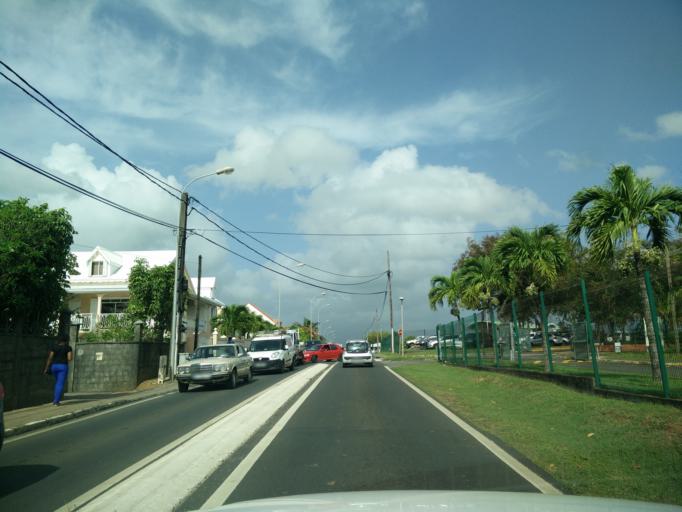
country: GP
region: Guadeloupe
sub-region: Guadeloupe
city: Baie-Mahault
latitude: 16.2411
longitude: -61.5932
